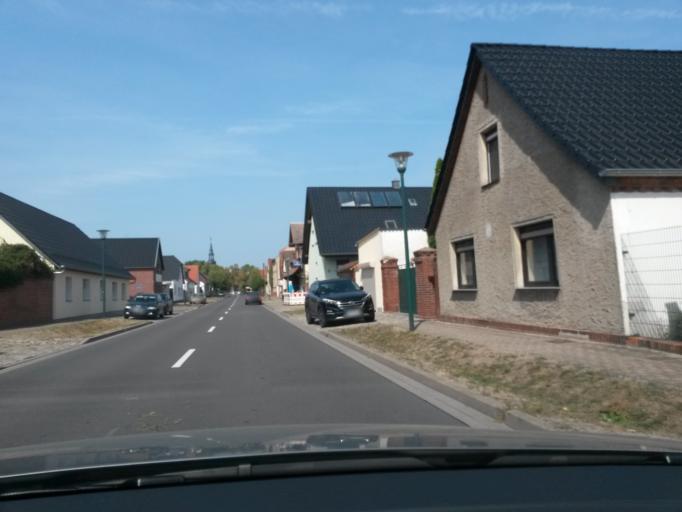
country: DE
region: Saxony-Anhalt
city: Rogatz
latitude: 52.2634
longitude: 11.7584
